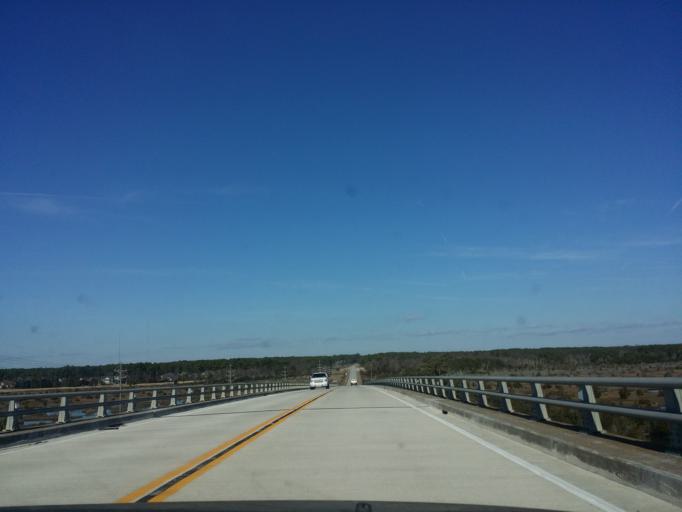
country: US
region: North Carolina
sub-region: Onslow County
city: Sneads Ferry
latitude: 34.5008
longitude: -77.4297
